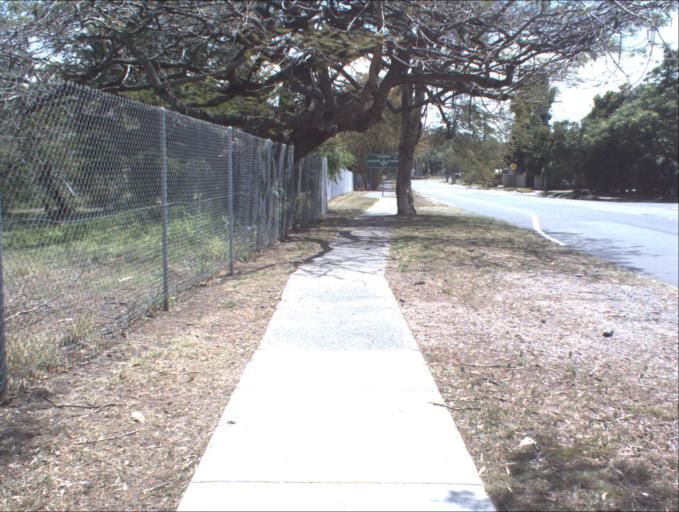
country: AU
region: Queensland
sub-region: Logan
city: Rochedale South
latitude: -27.5895
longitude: 153.1230
